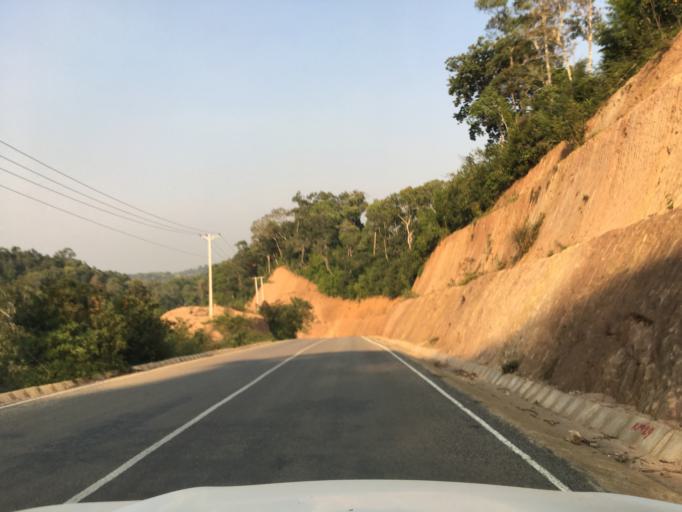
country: LA
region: Houaphan
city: Xam Nua
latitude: 20.5880
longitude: 104.0615
